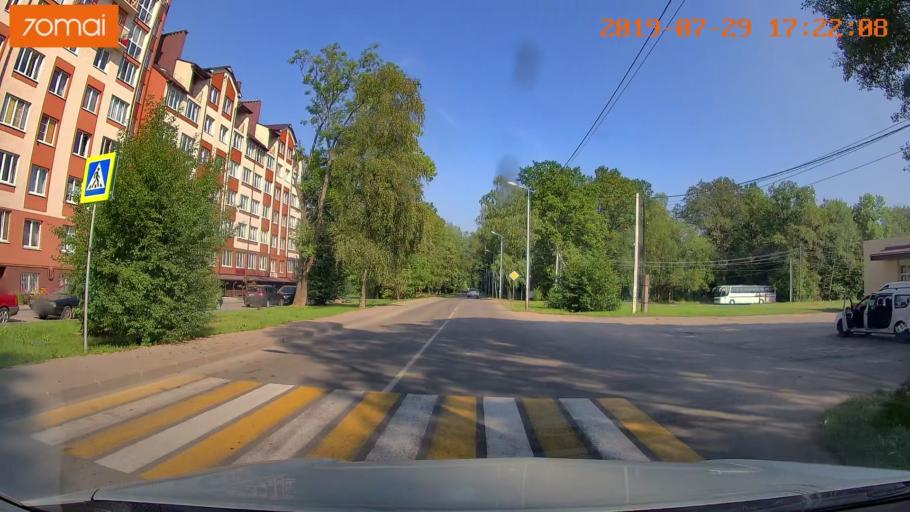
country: RU
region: Kaliningrad
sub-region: Gorod Kaliningrad
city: Kaliningrad
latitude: 54.7696
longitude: 20.4385
